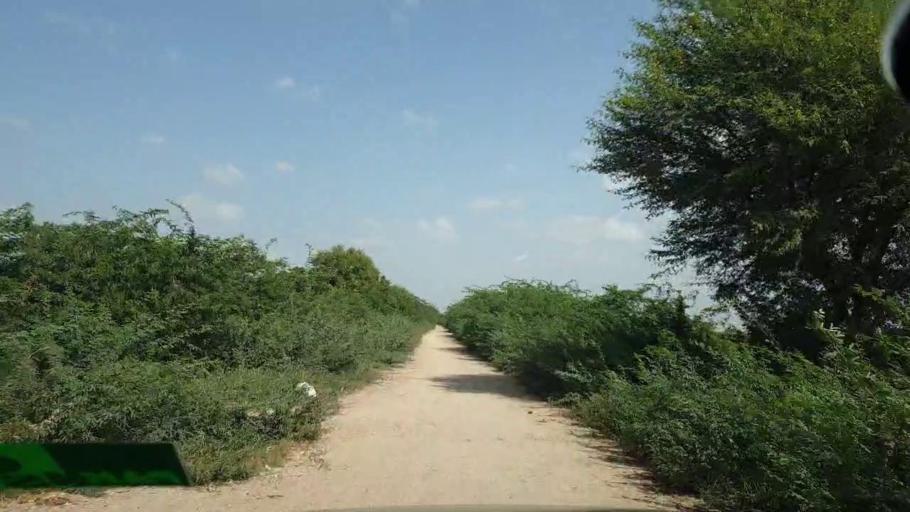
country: PK
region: Sindh
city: Naukot
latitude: 24.6448
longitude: 69.2324
